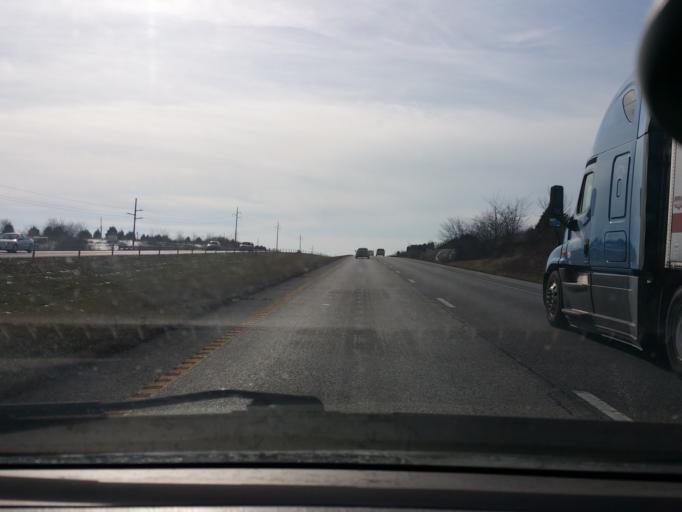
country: US
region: Missouri
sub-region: Clay County
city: Kearney
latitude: 39.3407
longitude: -94.3871
